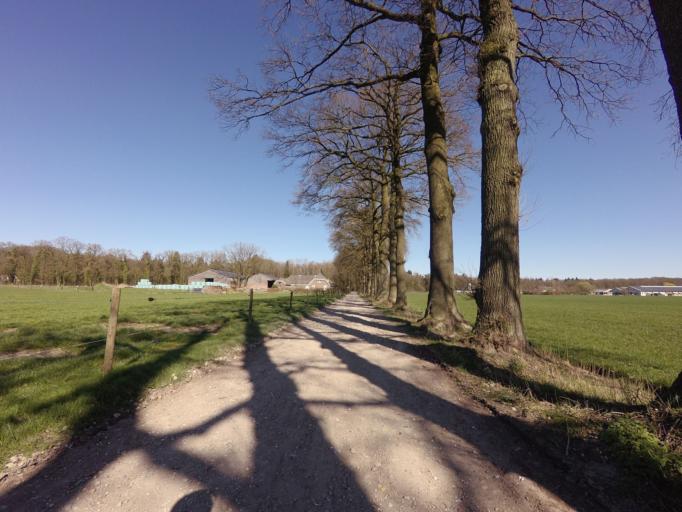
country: NL
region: Utrecht
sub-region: Gemeente Utrechtse Heuvelrug
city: Doorn
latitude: 52.0270
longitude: 5.3257
